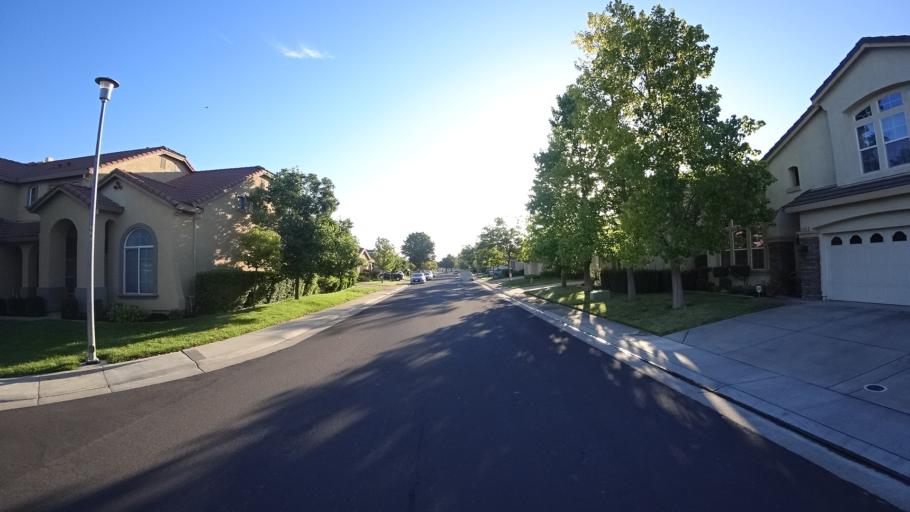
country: US
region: California
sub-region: Sacramento County
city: Laguna
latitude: 38.3967
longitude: -121.4771
